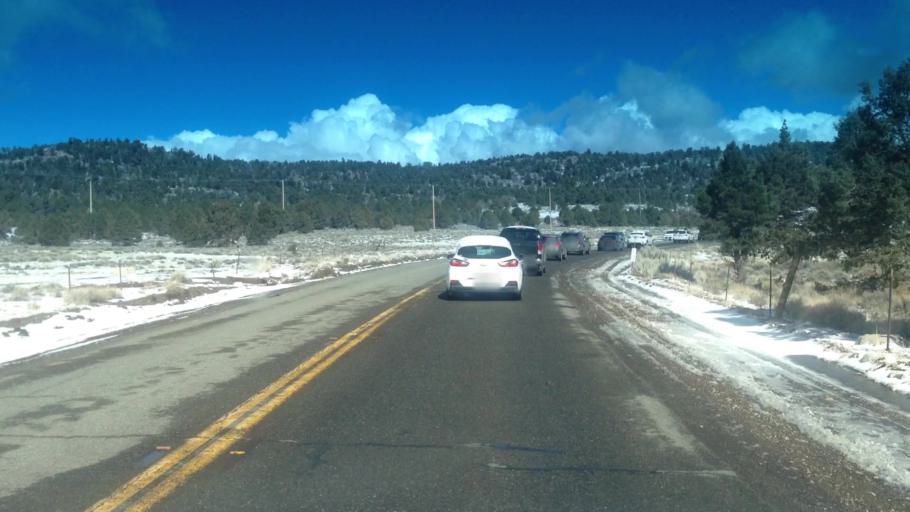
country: US
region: California
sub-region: San Bernardino County
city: Big Bear City
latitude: 34.2925
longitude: -116.8188
